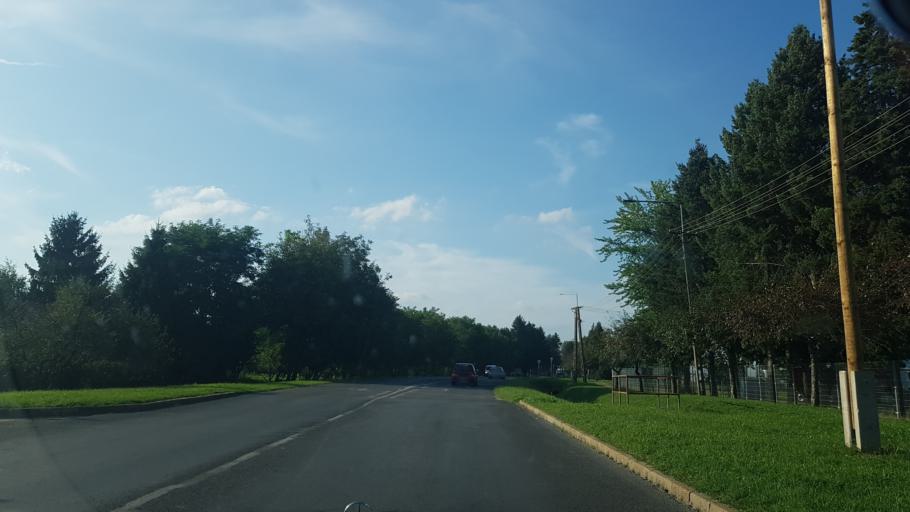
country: HU
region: Somogy
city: Nagyatad
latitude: 46.2396
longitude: 17.3560
